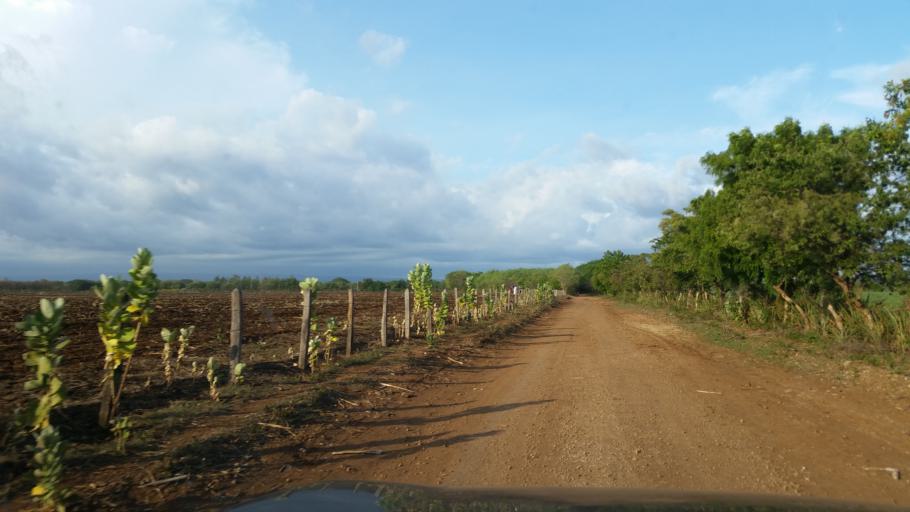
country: NI
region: Managua
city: Masachapa
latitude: 11.7756
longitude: -86.4837
